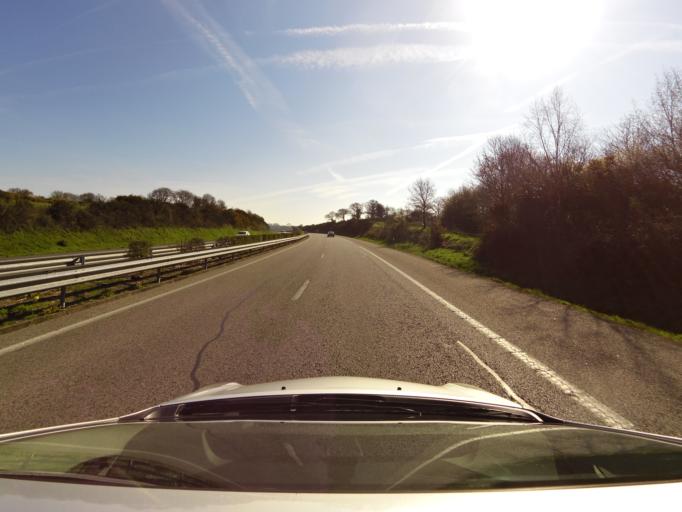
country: FR
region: Brittany
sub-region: Departement du Morbihan
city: Augan
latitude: 47.9236
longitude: -2.2312
